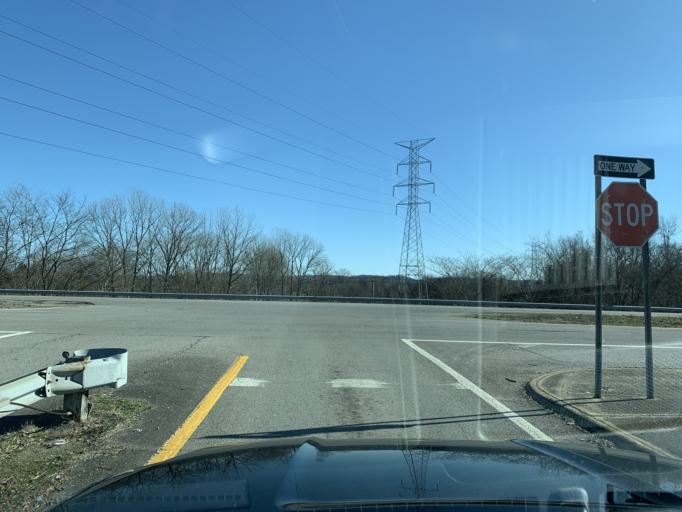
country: US
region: Tennessee
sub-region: Maury County
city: Mount Pleasant
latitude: 35.5193
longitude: -87.2232
